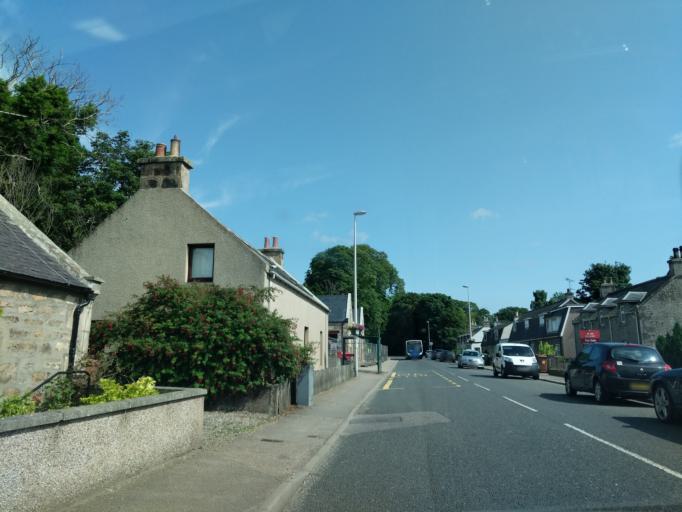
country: GB
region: Scotland
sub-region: Moray
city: Lhanbryd
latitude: 57.6354
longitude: -3.2236
